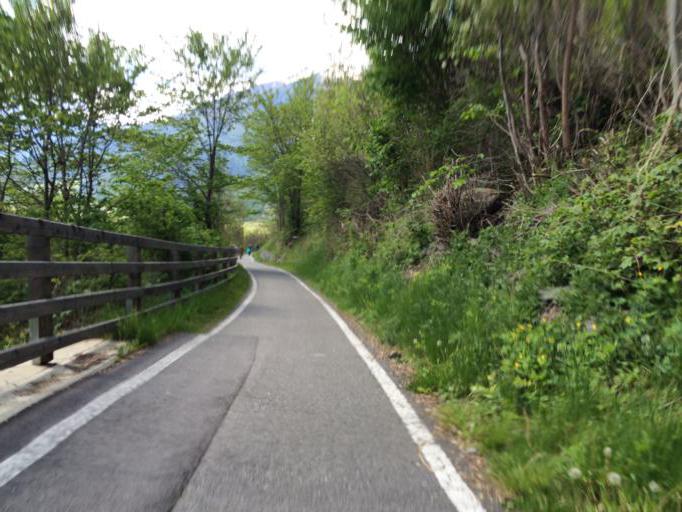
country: IT
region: Trentino-Alto Adige
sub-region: Bolzano
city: Malles Venosta
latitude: 46.7025
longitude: 10.5248
